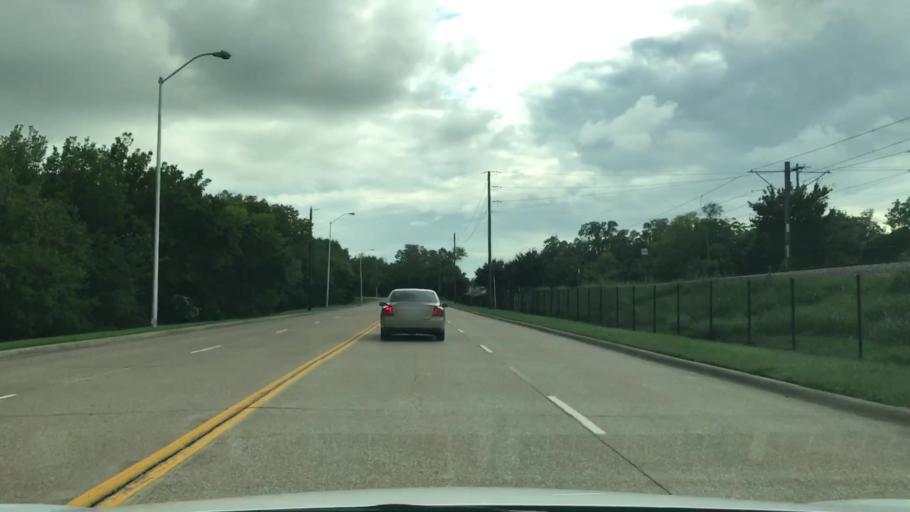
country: US
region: Texas
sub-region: Dallas County
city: Richardson
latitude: 32.9134
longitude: -96.7565
